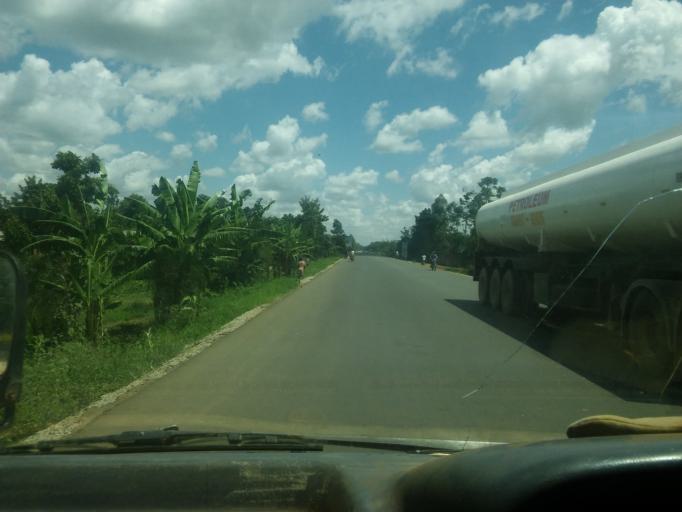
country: UG
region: Eastern Region
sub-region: Mbale District
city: Mbale
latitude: 1.0776
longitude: 34.1435
